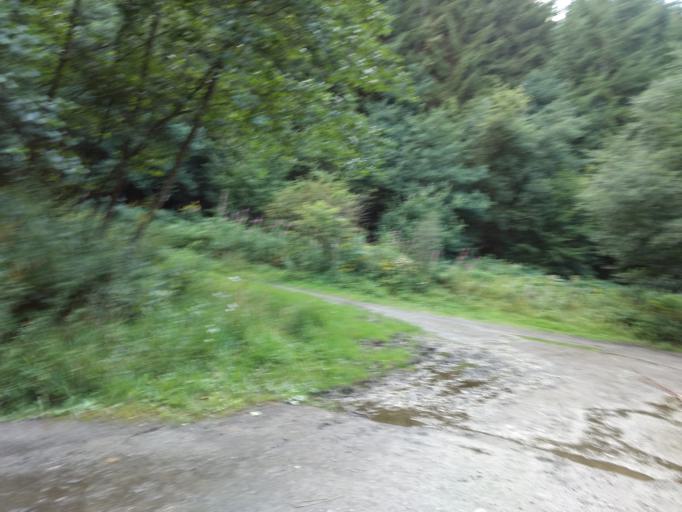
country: BE
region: Wallonia
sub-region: Province du Luxembourg
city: Houffalize
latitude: 50.1483
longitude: 5.7274
